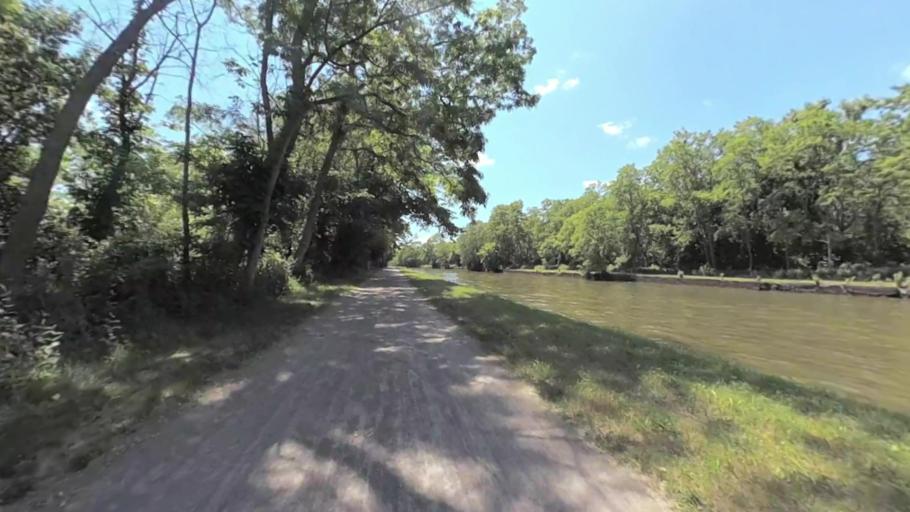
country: US
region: New York
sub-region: Monroe County
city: Pittsford
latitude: 43.0672
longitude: -77.4882
